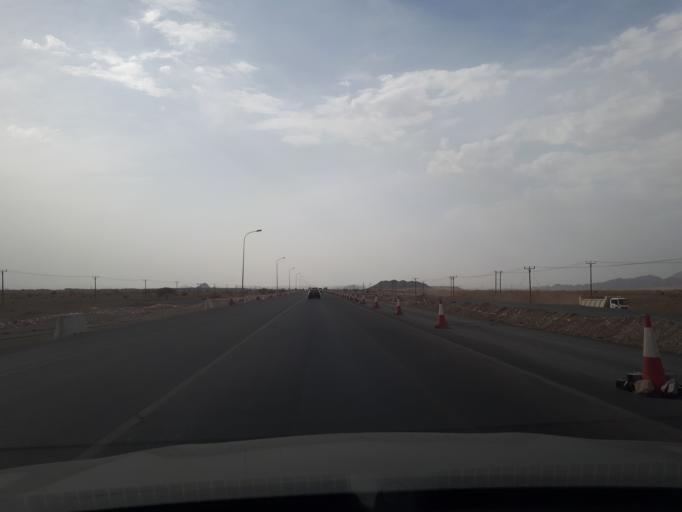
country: OM
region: Ash Sharqiyah
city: Al Qabil
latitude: 22.5453
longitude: 58.7229
